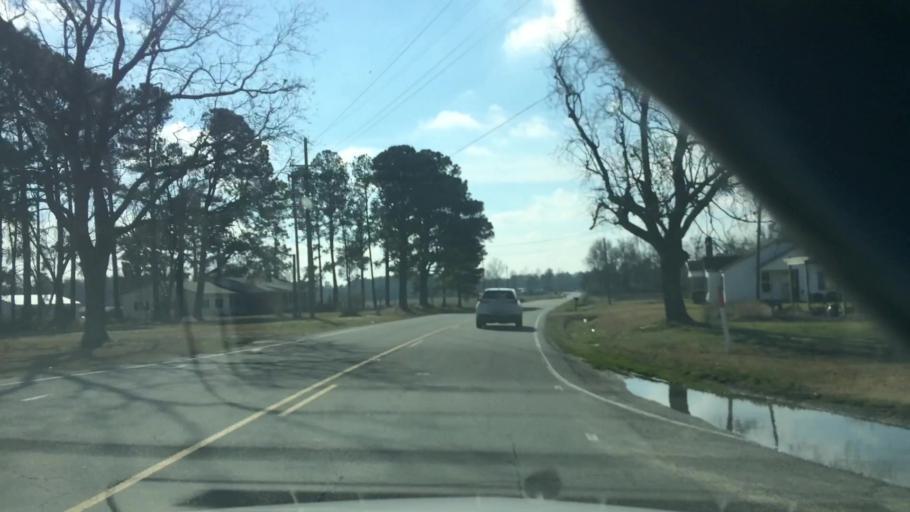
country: US
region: North Carolina
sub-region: Duplin County
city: Beulaville
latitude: 34.8870
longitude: -77.7848
